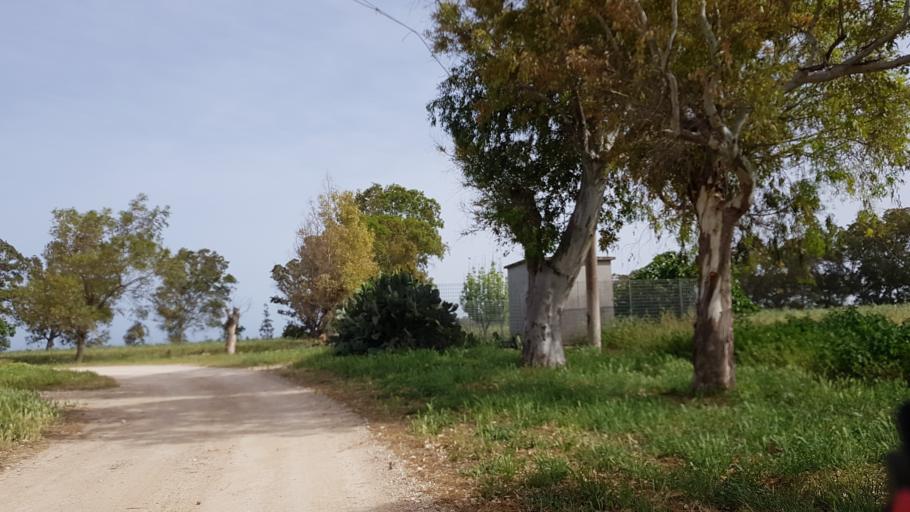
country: IT
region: Apulia
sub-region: Provincia di Brindisi
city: La Rosa
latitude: 40.5953
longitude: 18.0311
